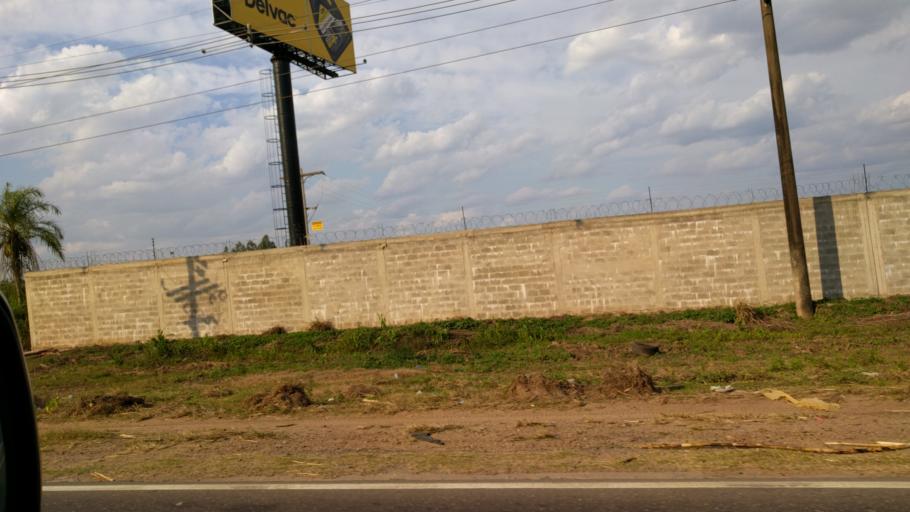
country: BO
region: Santa Cruz
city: La Belgica
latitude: -17.5618
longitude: -63.1592
